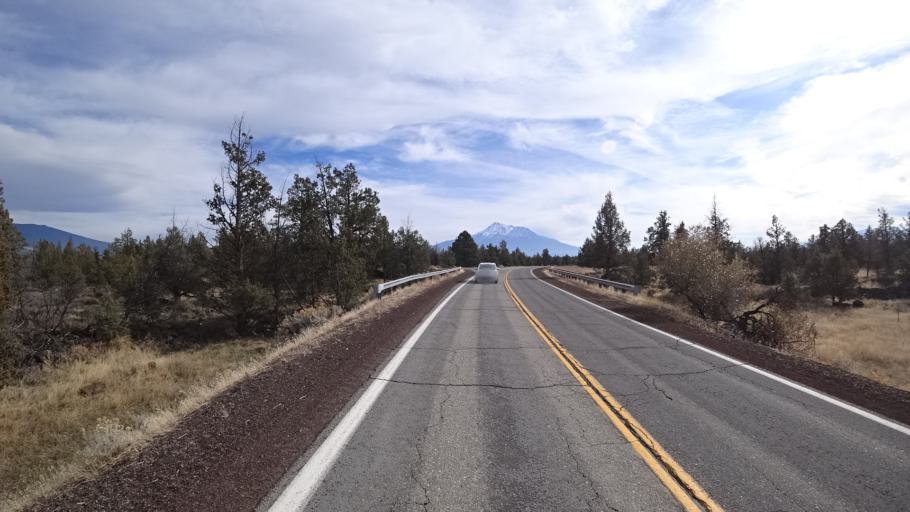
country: US
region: California
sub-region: Siskiyou County
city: Montague
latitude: 41.6063
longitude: -122.3954
